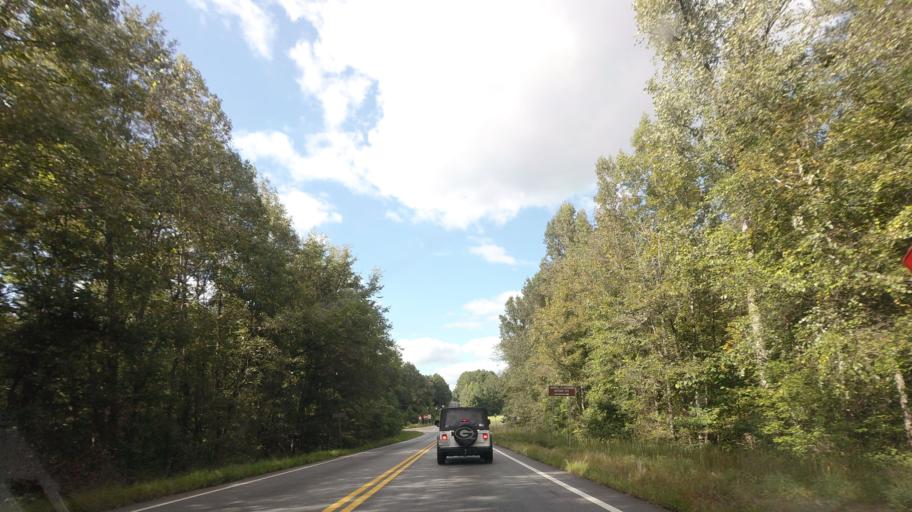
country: US
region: Georgia
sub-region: Monroe County
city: Forsyth
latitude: 33.0228
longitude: -83.7448
